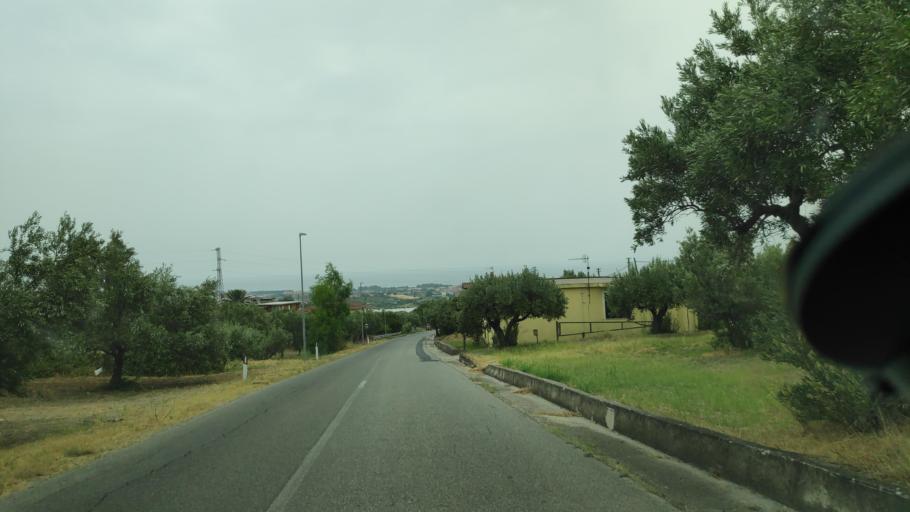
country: IT
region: Calabria
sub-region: Provincia di Catanzaro
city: Martelli-Laganosa
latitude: 38.6666
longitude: 16.5150
